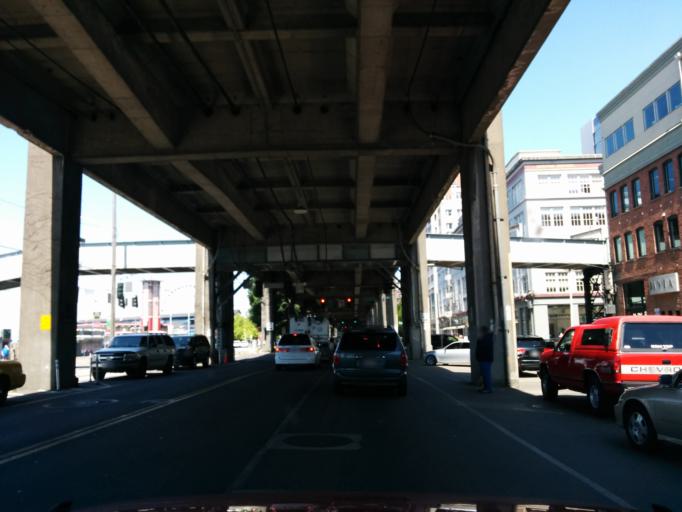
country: US
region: Washington
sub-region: King County
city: Seattle
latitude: 47.6027
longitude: -122.3370
